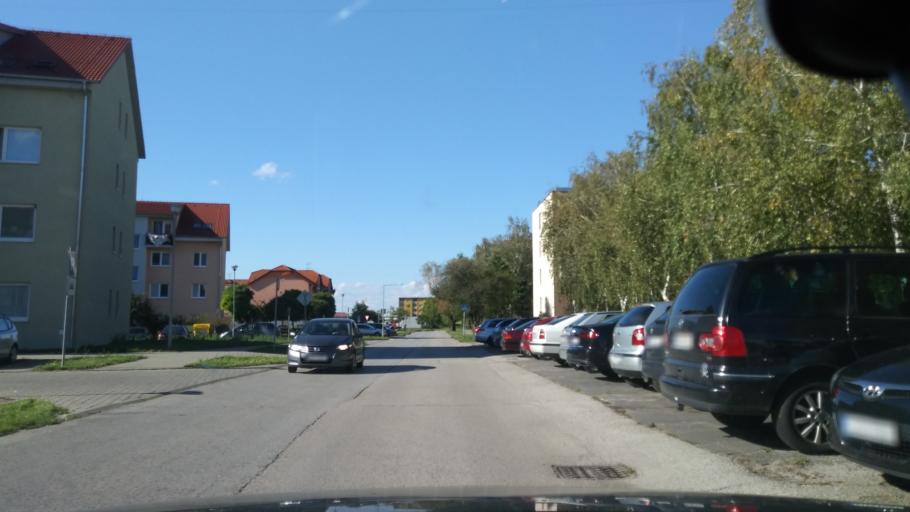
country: SK
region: Trnavsky
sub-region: Okres Skalica
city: Skalica
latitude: 48.8373
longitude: 17.2238
